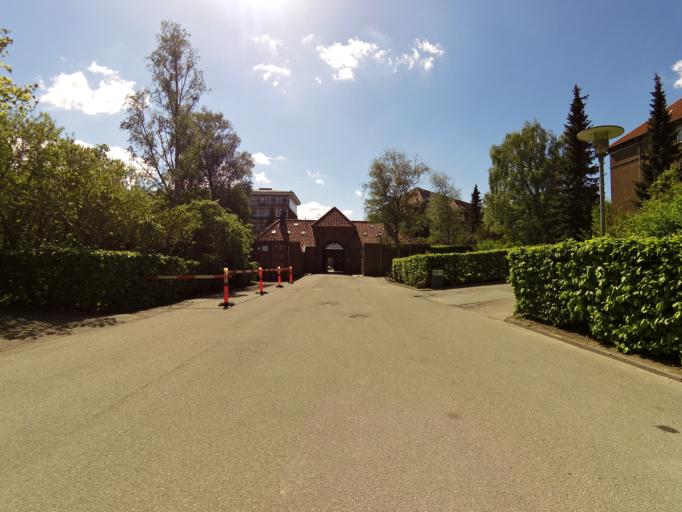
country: DK
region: Capital Region
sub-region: Frederiksberg Kommune
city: Frederiksberg
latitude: 55.7128
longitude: 12.5387
